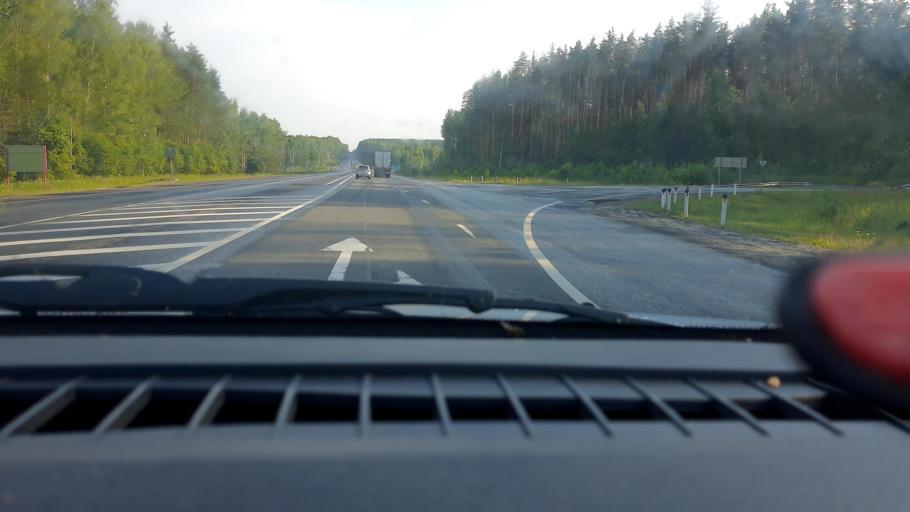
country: RU
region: Nizjnij Novgorod
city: Arzamas
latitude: 55.5023
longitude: 43.8942
